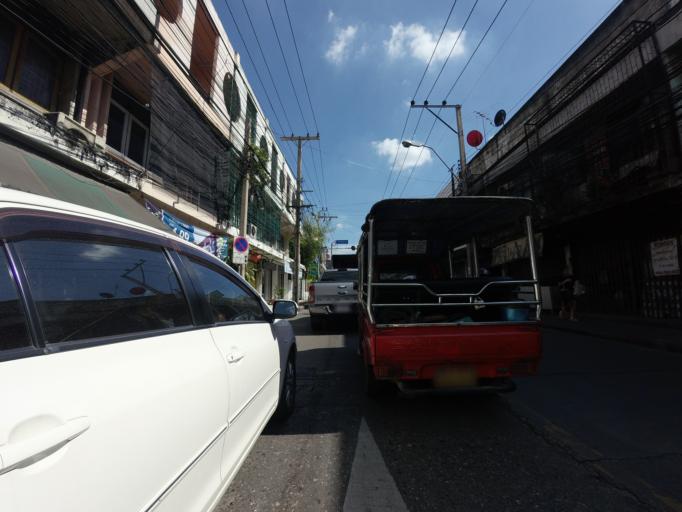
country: TH
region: Bangkok
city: Lat Phrao
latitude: 13.7996
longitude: 100.5960
